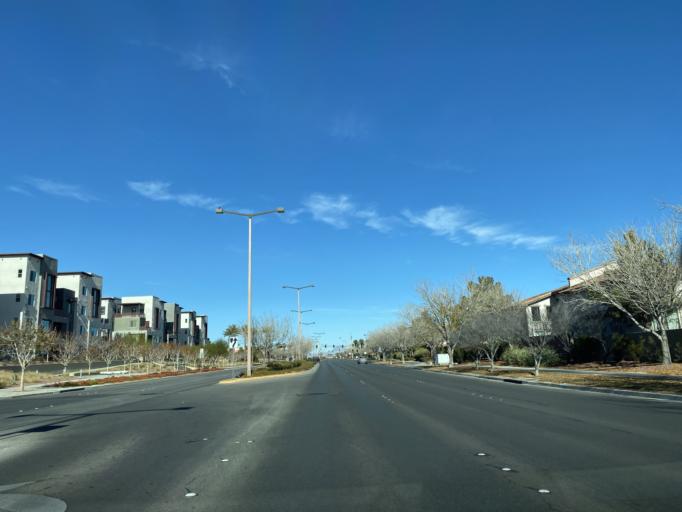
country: US
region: Nevada
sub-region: Clark County
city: Summerlin South
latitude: 36.1550
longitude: -115.3230
